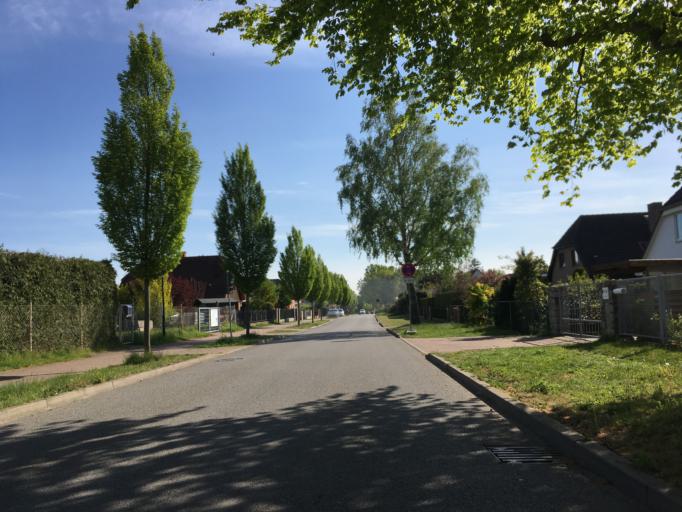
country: DE
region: Berlin
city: Buch
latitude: 52.6615
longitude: 13.5226
